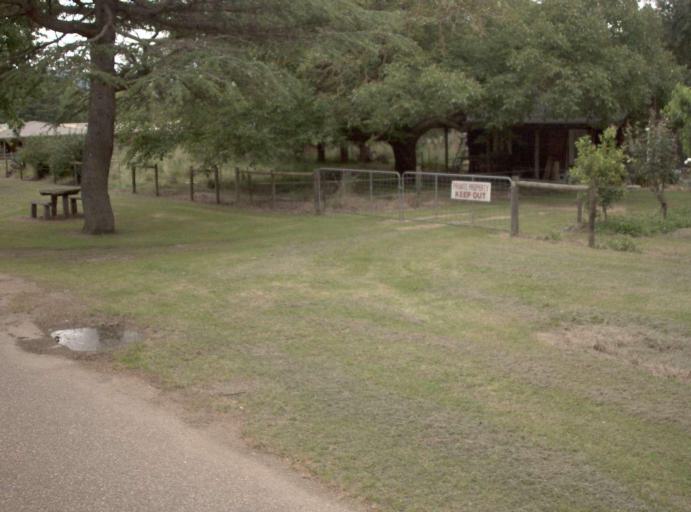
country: AU
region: Victoria
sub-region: East Gippsland
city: Bairnsdale
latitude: -37.4657
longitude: 147.2512
